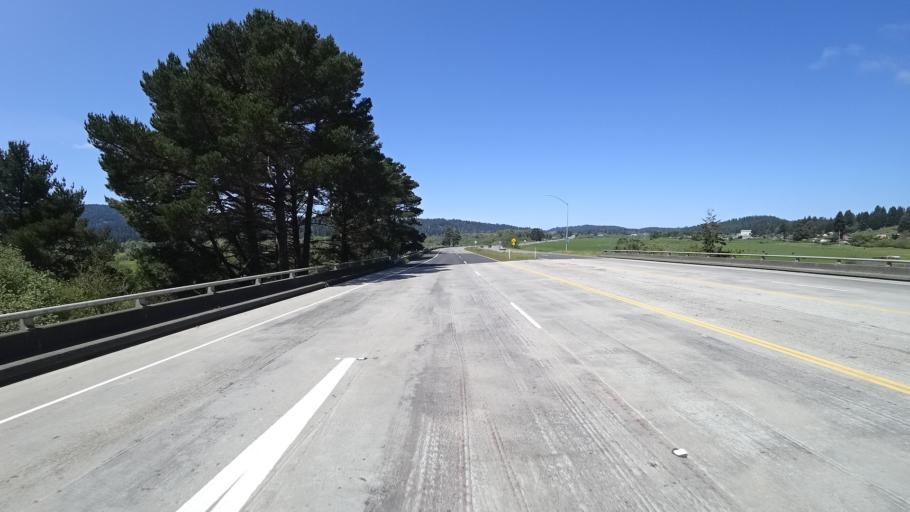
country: US
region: California
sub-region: Humboldt County
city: Blue Lake
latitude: 40.8883
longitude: -124.0007
